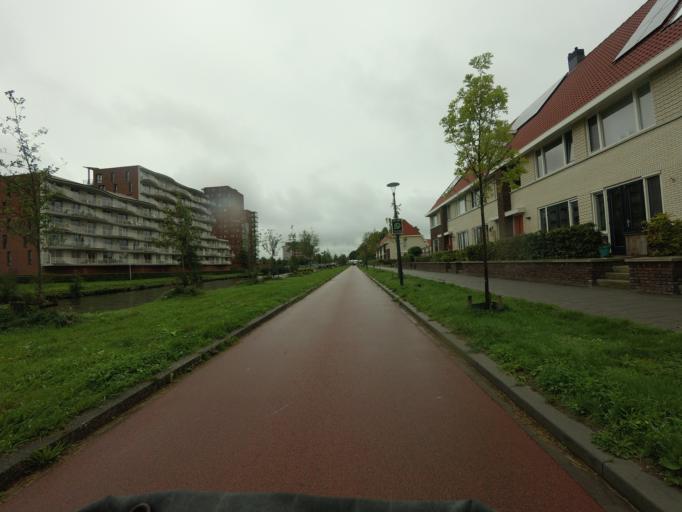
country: NL
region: Friesland
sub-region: Gemeente Leeuwarden
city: Bilgaard
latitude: 53.2147
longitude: 5.8043
